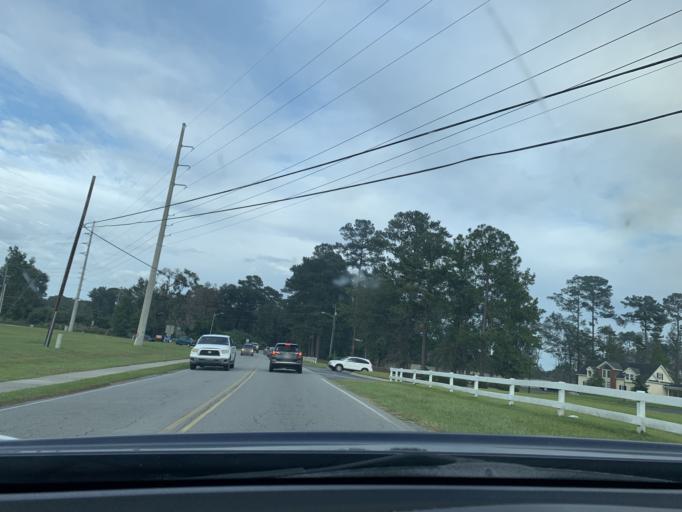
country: US
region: Georgia
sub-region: Chatham County
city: Pooler
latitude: 32.0925
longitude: -81.2582
